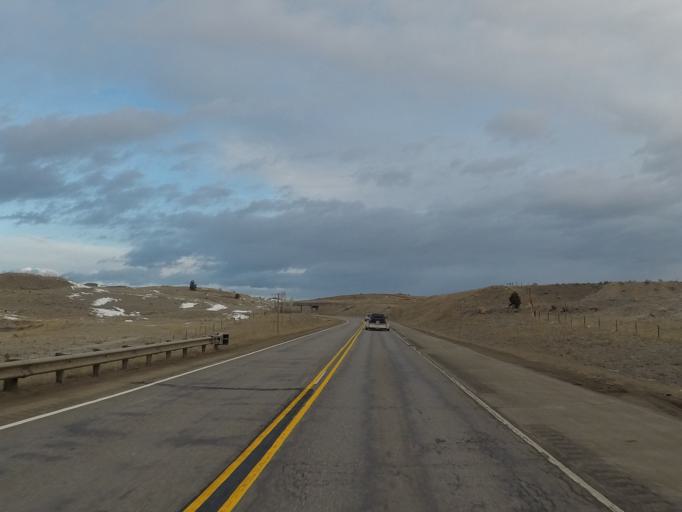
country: US
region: Montana
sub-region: Silver Bow County
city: Butte
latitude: 46.0001
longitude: -112.5661
